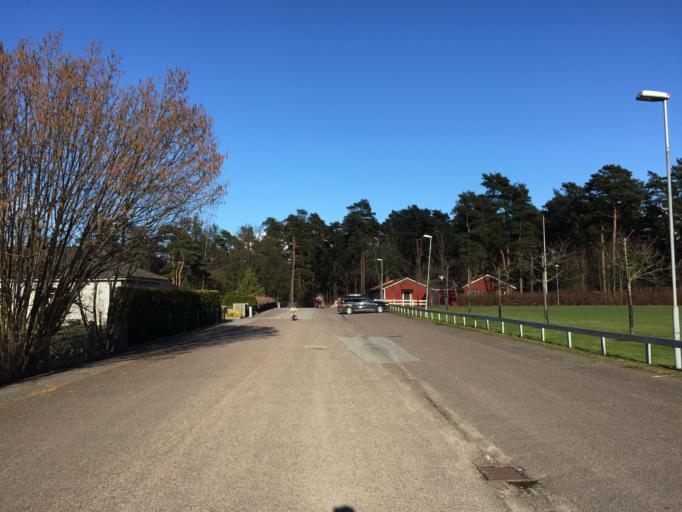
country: SE
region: Skane
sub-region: Lunds Kommun
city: Veberod
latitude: 55.6341
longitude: 13.5022
